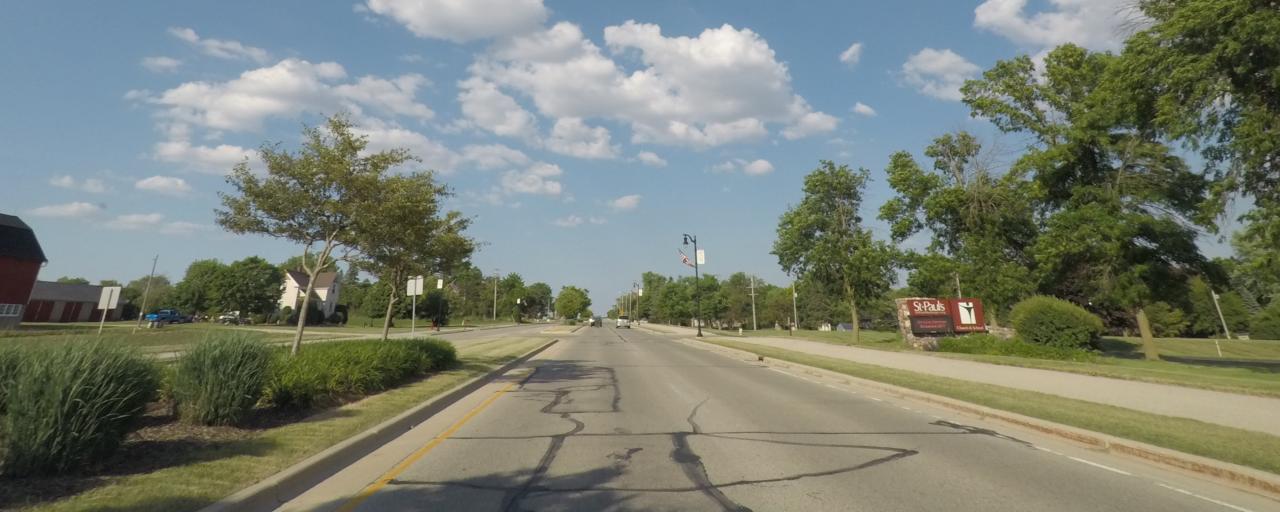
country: US
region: Wisconsin
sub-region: Milwaukee County
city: Hales Corners
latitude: 42.9255
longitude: -88.0914
